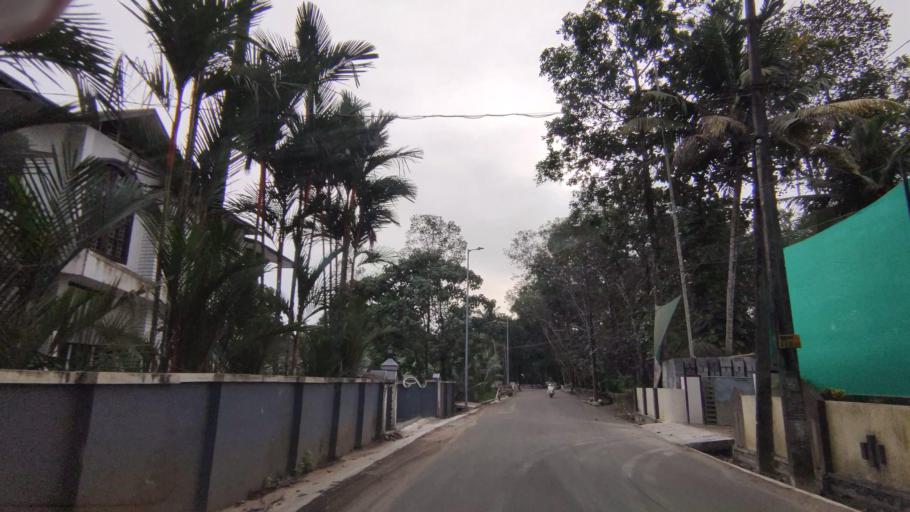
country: IN
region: Kerala
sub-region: Kottayam
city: Kottayam
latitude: 9.6650
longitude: 76.5269
